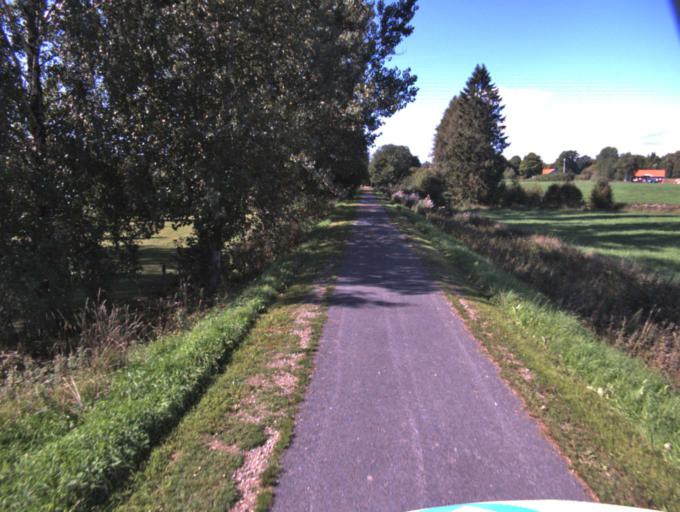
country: SE
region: Vaestra Goetaland
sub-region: Ulricehamns Kommun
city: Ulricehamn
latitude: 57.8008
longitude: 13.3751
